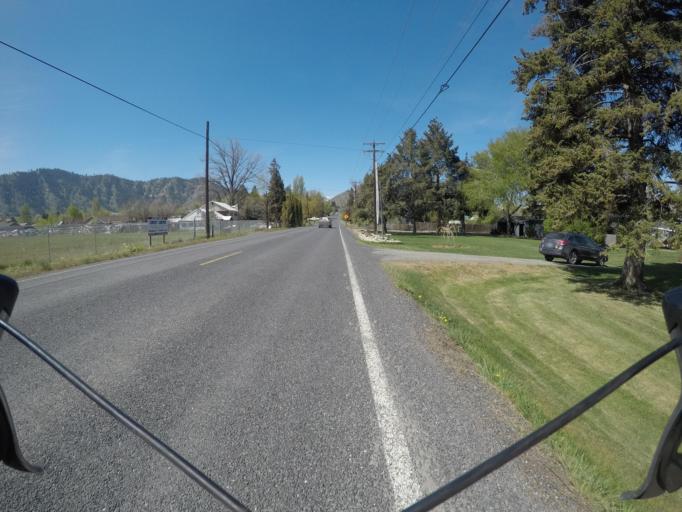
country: US
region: Washington
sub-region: Chelan County
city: Cashmere
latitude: 47.5245
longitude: -120.4910
